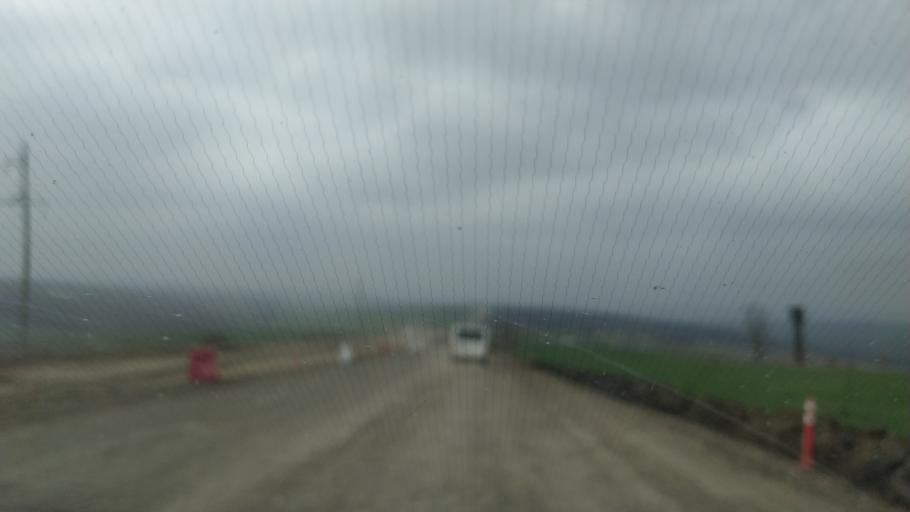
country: MD
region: Gagauzia
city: Comrat
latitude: 46.3217
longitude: 28.7235
